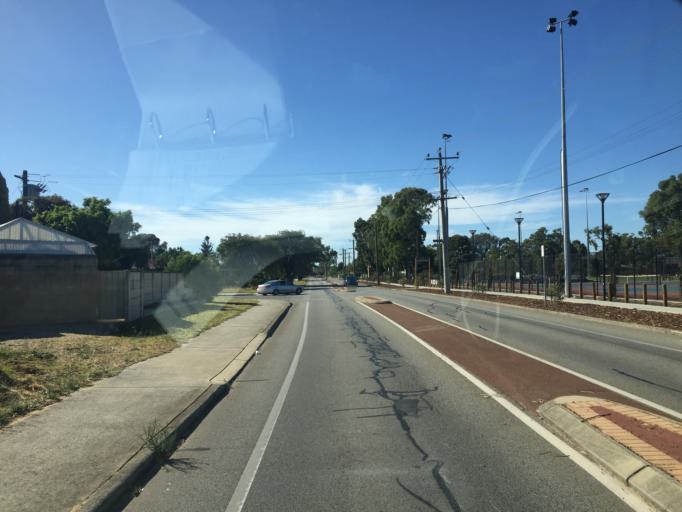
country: AU
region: Western Australia
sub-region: Gosnells
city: Kenwick
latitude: -32.0232
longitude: 115.9655
